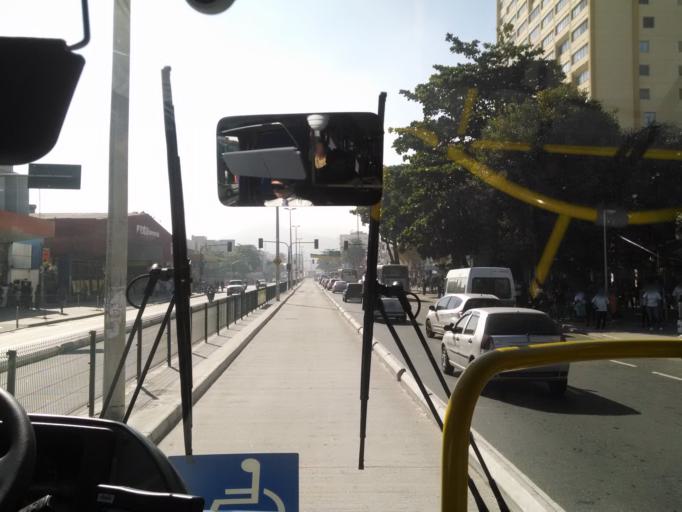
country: BR
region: Rio de Janeiro
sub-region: Sao Joao De Meriti
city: Sao Joao de Meriti
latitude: -22.9224
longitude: -43.3721
